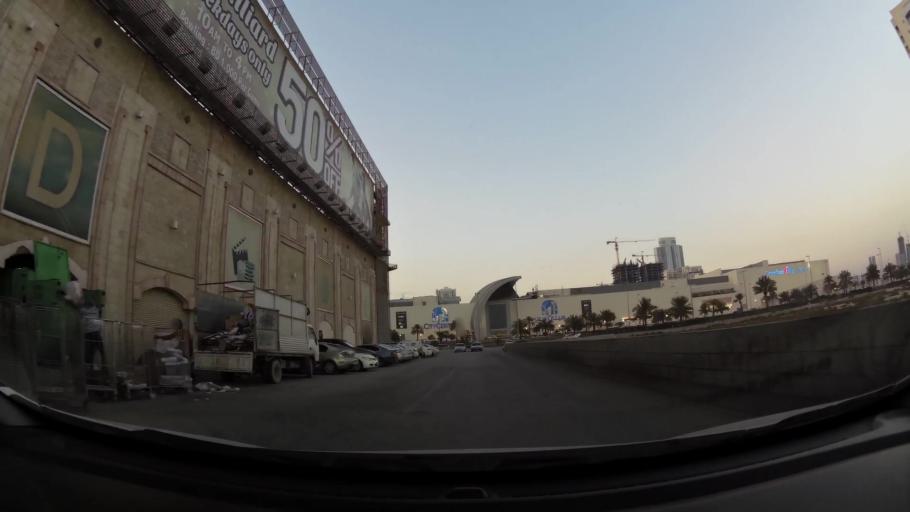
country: BH
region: Manama
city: Jidd Hafs
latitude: 26.2304
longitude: 50.5536
